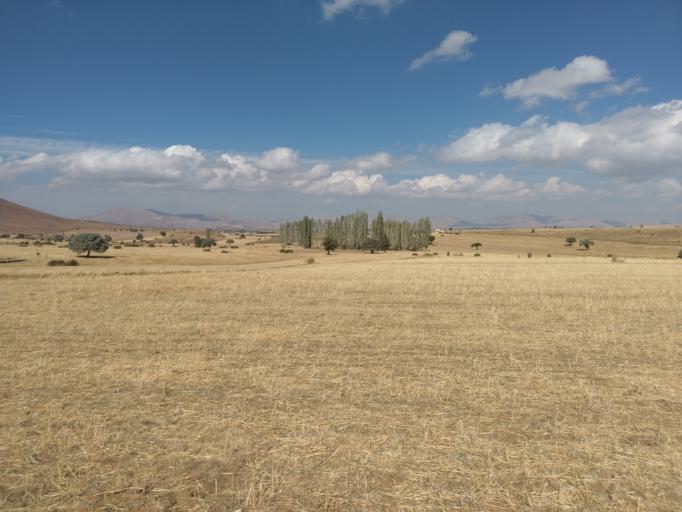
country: TR
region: Kayseri
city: Toklar
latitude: 38.3973
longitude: 36.0911
